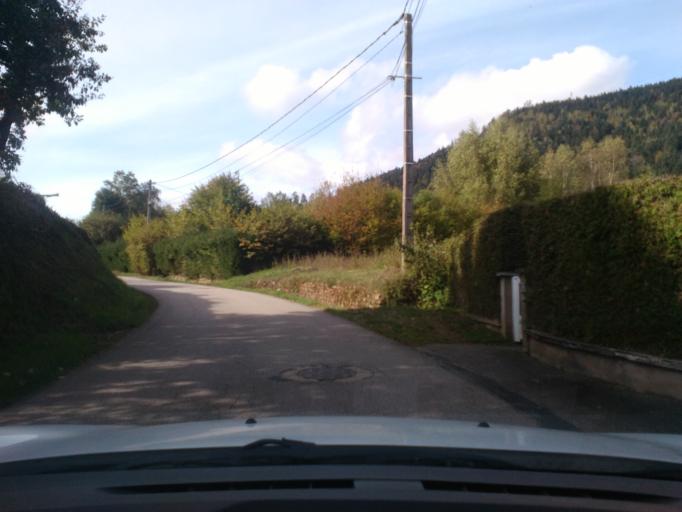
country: FR
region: Lorraine
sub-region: Departement des Vosges
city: Sainte-Marguerite
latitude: 48.2970
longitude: 7.0106
